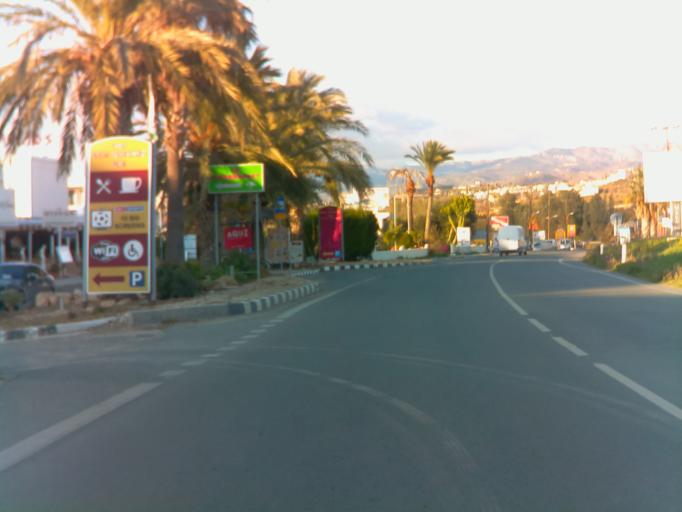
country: CY
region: Pafos
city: Kissonerga
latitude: 34.8101
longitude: 32.3961
